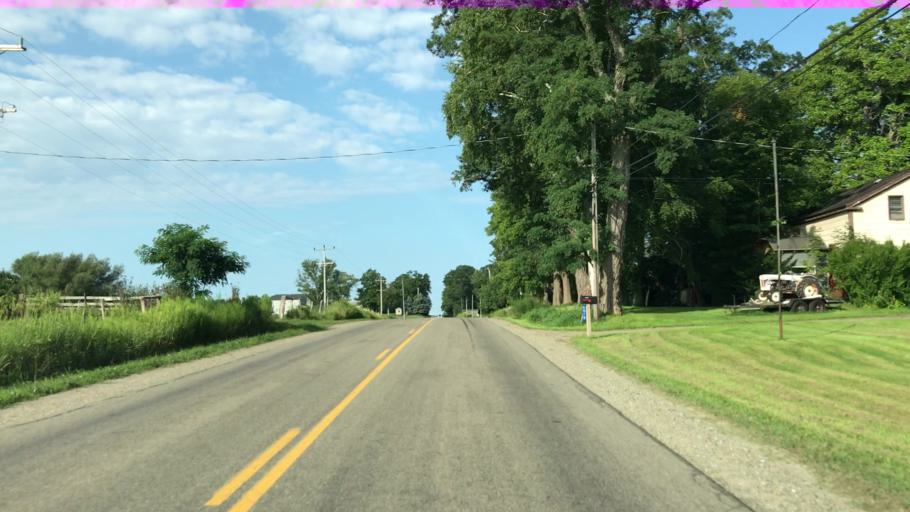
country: US
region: New York
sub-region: Chautauqua County
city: Mayville
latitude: 42.2767
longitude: -79.4515
